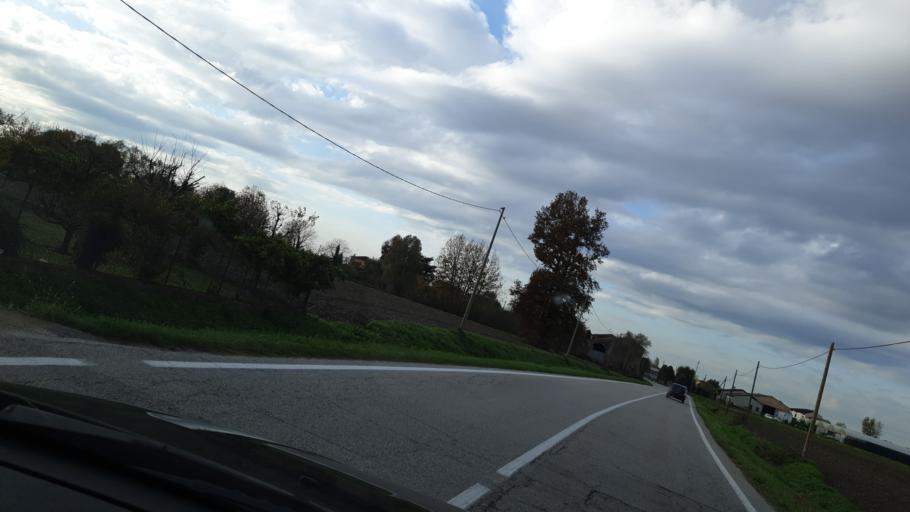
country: IT
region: Veneto
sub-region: Provincia di Rovigo
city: Lendinara
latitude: 45.0714
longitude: 11.6203
